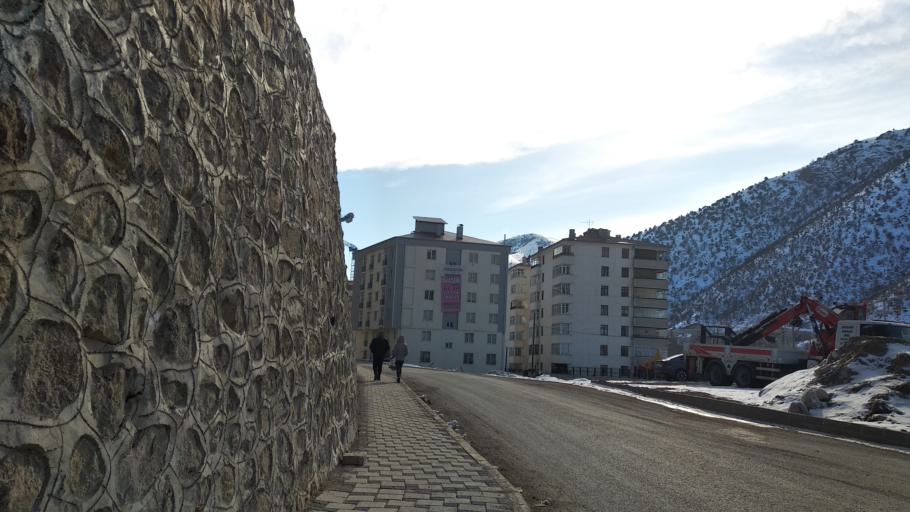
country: TR
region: Gumushane
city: Gumushkhane
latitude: 40.4398
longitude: 39.5042
